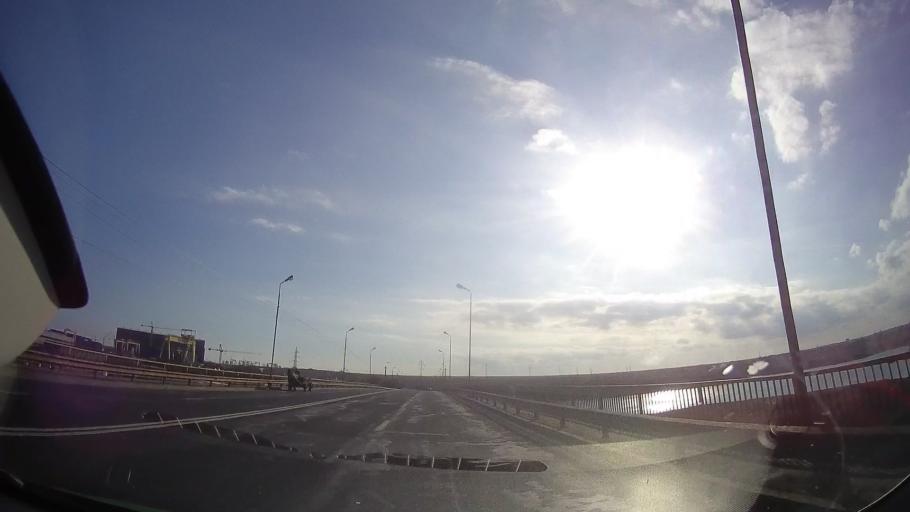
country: RO
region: Constanta
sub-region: Municipiul Mangalia
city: Mangalia
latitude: 43.8035
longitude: 28.5601
